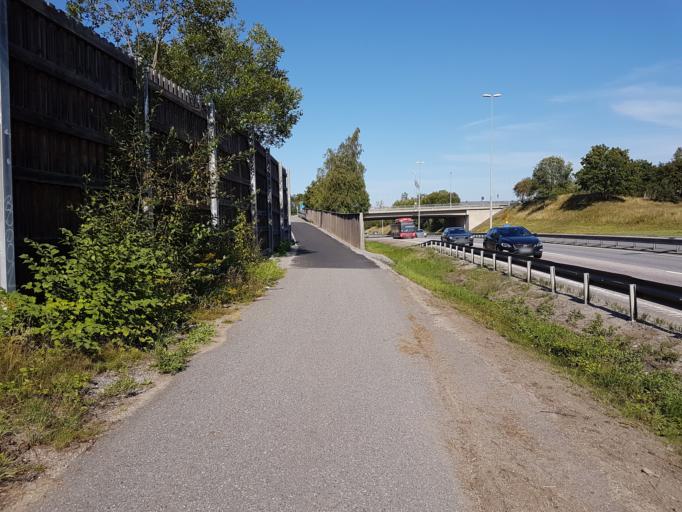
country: SE
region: Stockholm
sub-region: Huddinge Kommun
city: Huddinge
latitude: 59.2344
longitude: 17.9734
